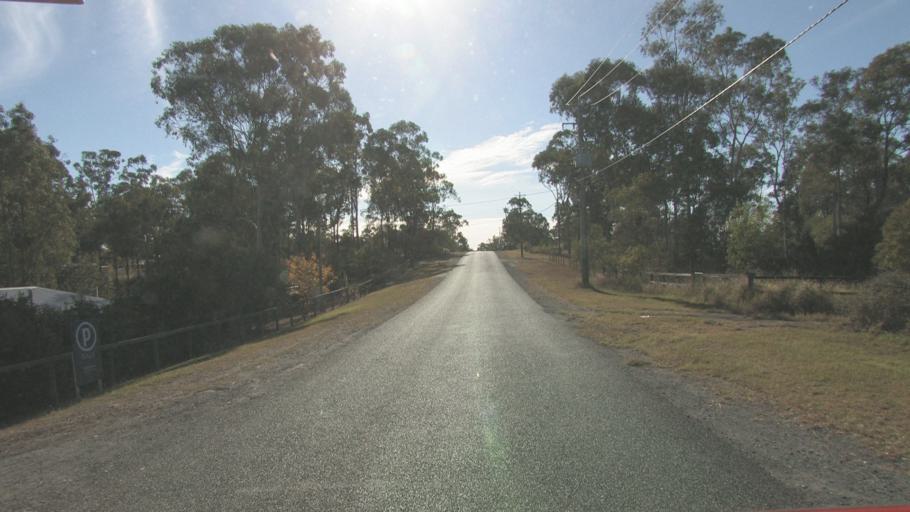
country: AU
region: Queensland
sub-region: Ipswich
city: Springfield Lakes
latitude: -27.7049
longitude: 152.9264
